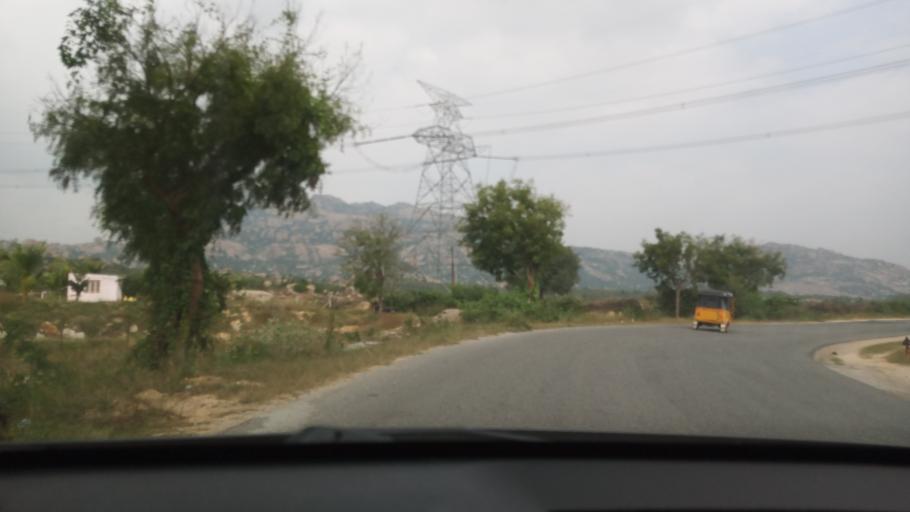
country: IN
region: Andhra Pradesh
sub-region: Chittoor
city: Pakala
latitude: 13.6564
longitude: 78.8363
